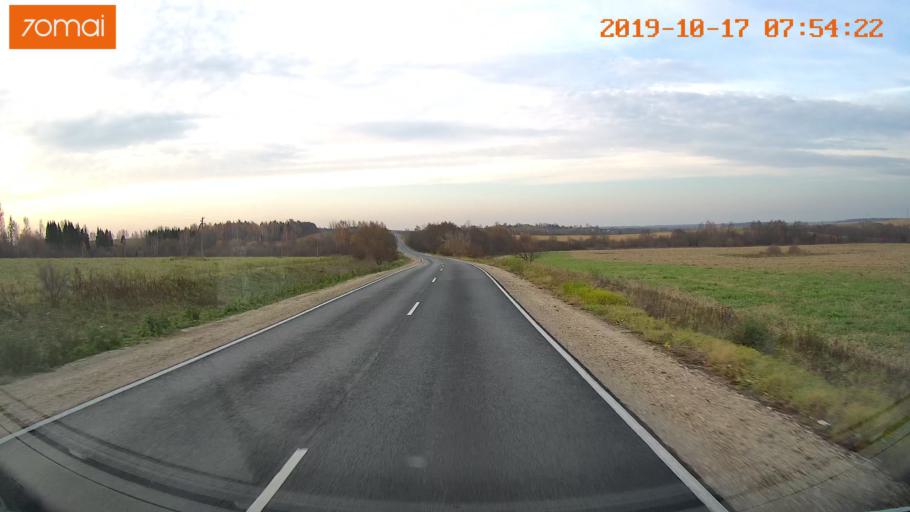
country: RU
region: Vladimir
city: Bavleny
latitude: 56.4507
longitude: 39.6071
